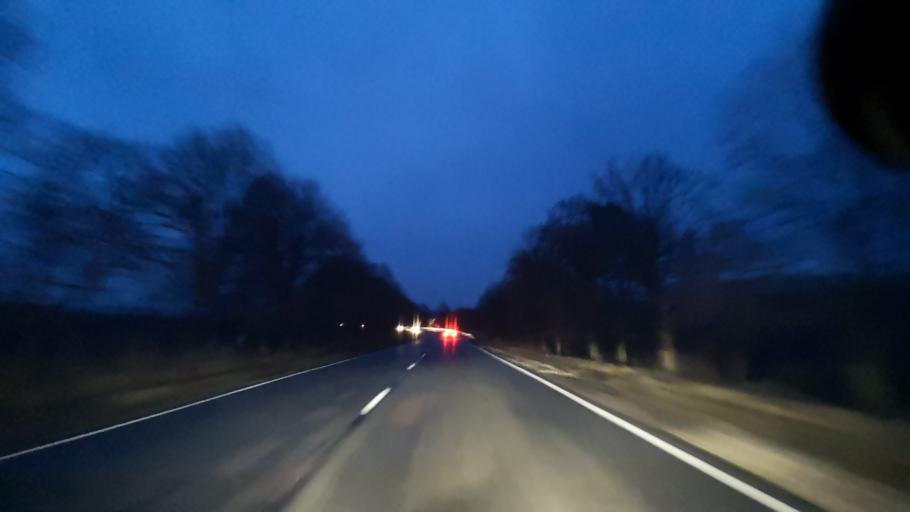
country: MD
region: Orhei
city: Orhei
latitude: 47.4722
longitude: 28.7919
